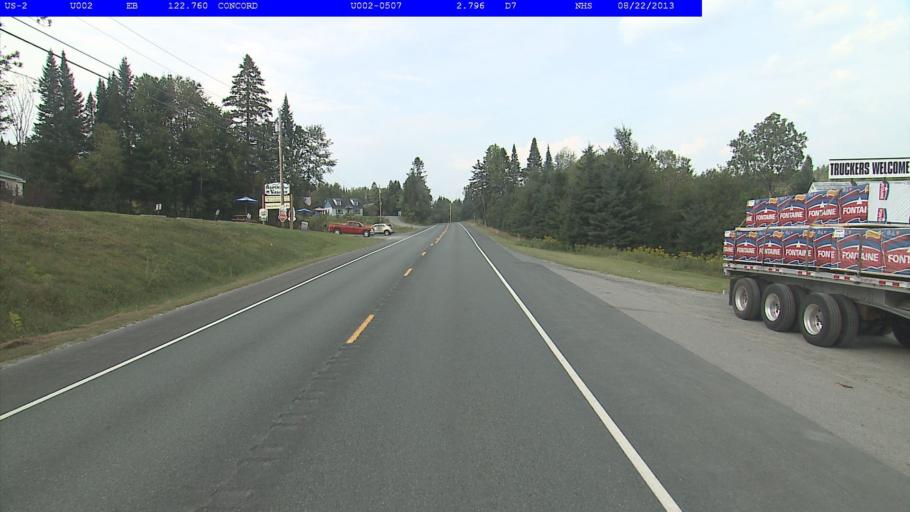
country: US
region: Vermont
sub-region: Caledonia County
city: St Johnsbury
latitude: 44.4347
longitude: -71.8794
